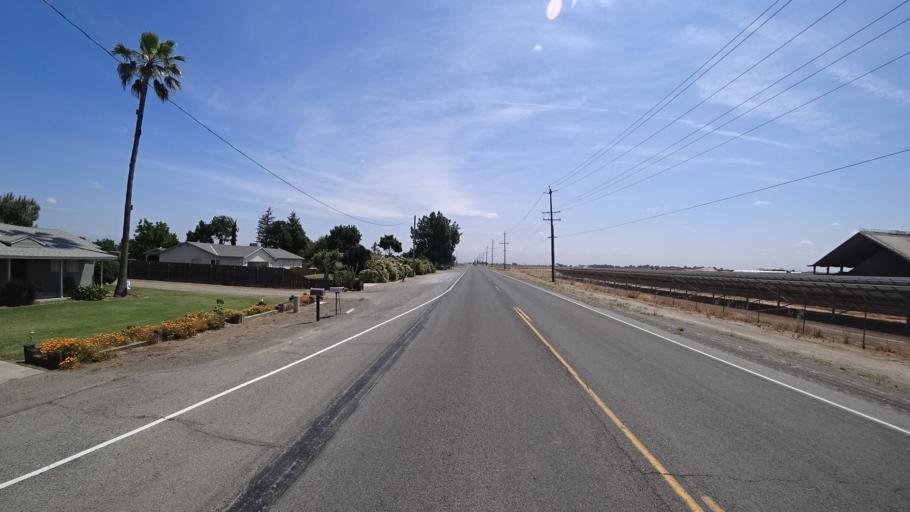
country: US
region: California
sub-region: Tulare County
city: Goshen
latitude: 36.2976
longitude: -119.4907
